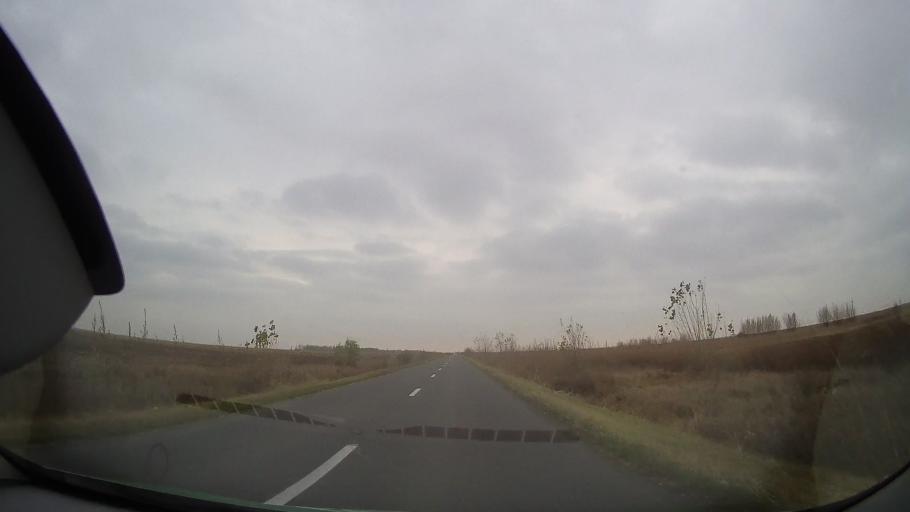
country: RO
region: Ialomita
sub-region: Comuna Garbovi
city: Garbovi
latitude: 44.7487
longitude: 26.7185
